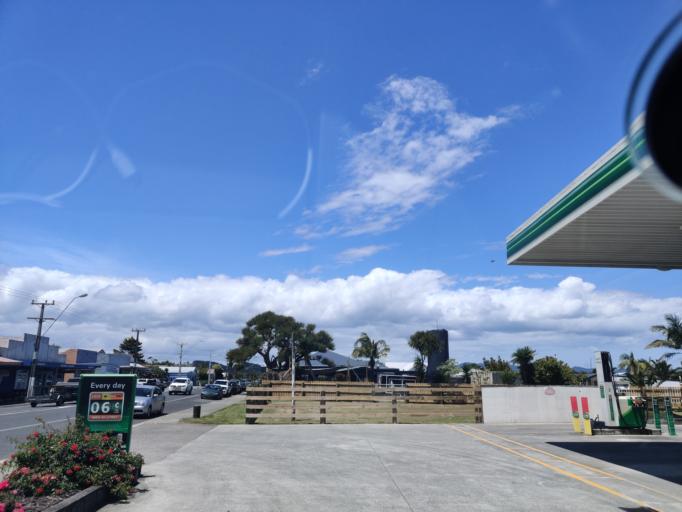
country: NZ
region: Northland
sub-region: Far North District
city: Kaitaia
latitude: -35.0476
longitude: 173.2560
